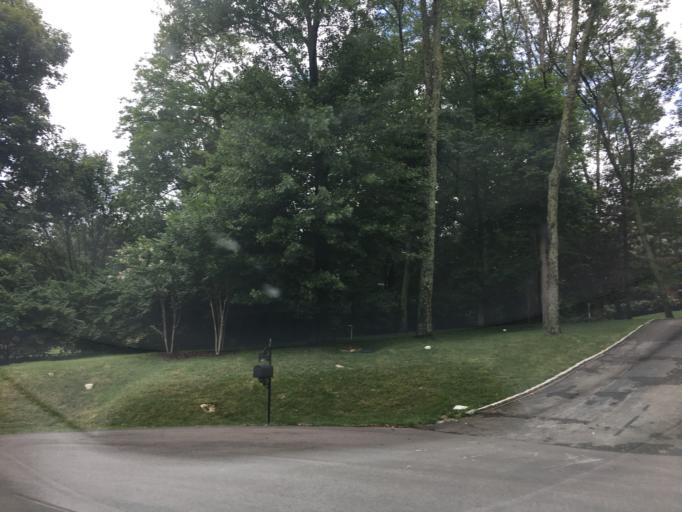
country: US
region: Tennessee
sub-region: Davidson County
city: Forest Hills
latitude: 36.0857
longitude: -86.8384
